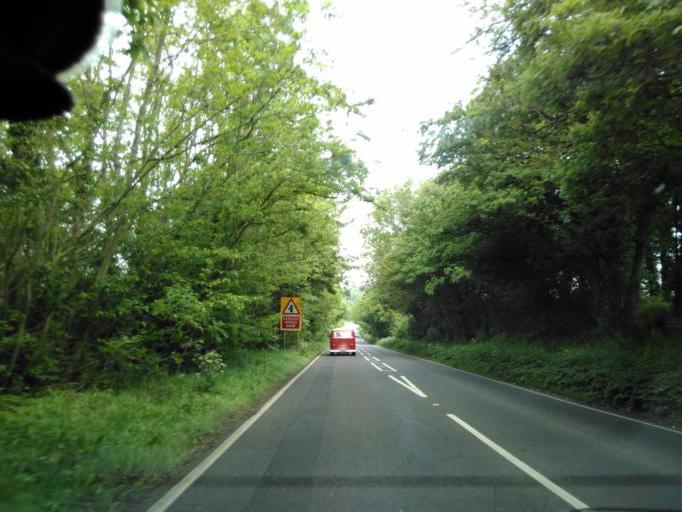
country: GB
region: England
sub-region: Kent
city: Chartham
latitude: 51.2292
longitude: 1.0620
